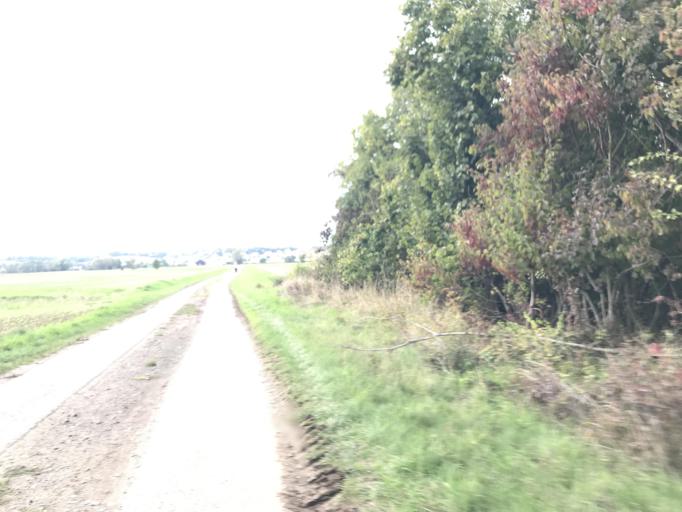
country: DE
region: Hesse
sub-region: Regierungsbezirk Kassel
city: Wabern
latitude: 51.0822
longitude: 9.3528
